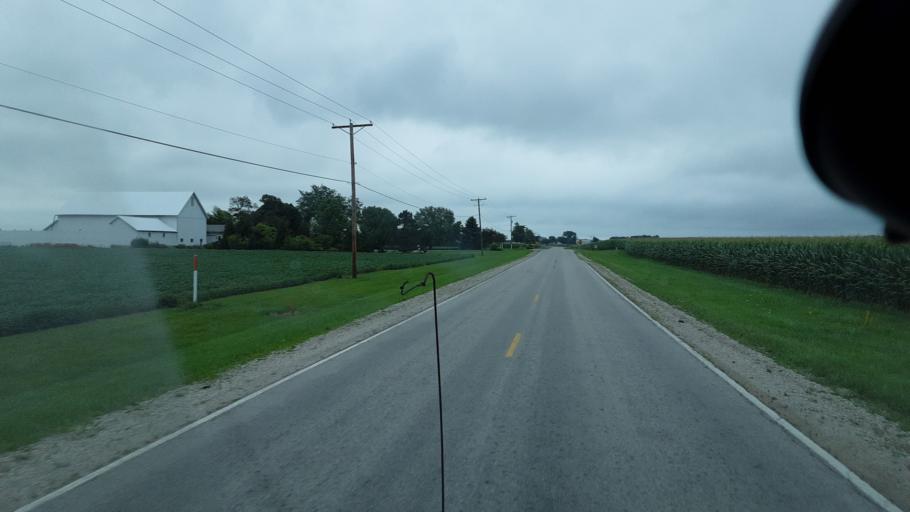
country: US
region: Indiana
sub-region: Wells County
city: Bluffton
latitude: 40.7489
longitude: -85.0902
